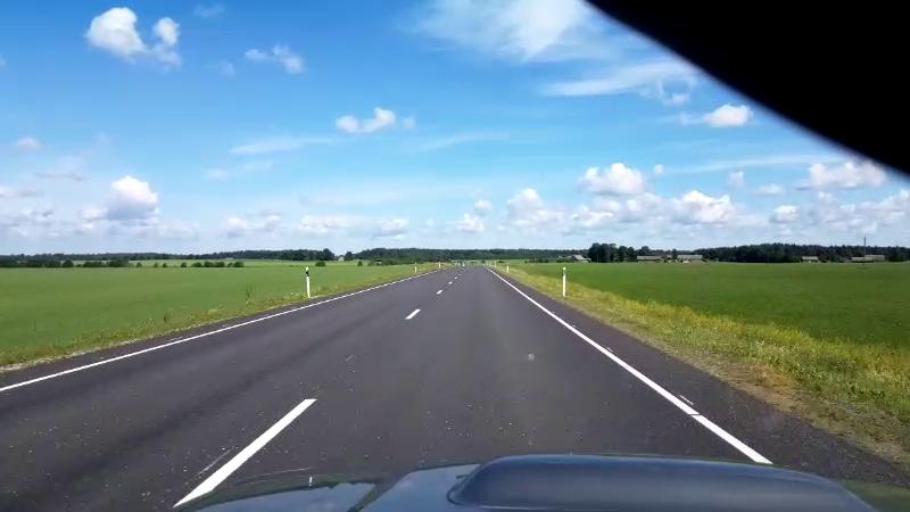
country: EE
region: Jaervamaa
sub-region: Jaerva-Jaani vald
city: Jarva-Jaani
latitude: 59.1444
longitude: 25.7710
